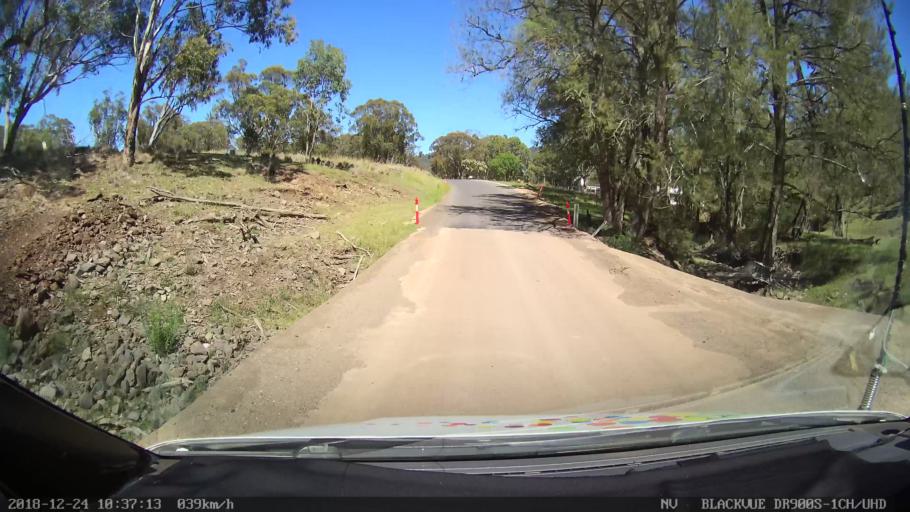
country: AU
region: New South Wales
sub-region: Upper Hunter Shire
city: Merriwa
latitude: -31.8460
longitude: 150.4946
